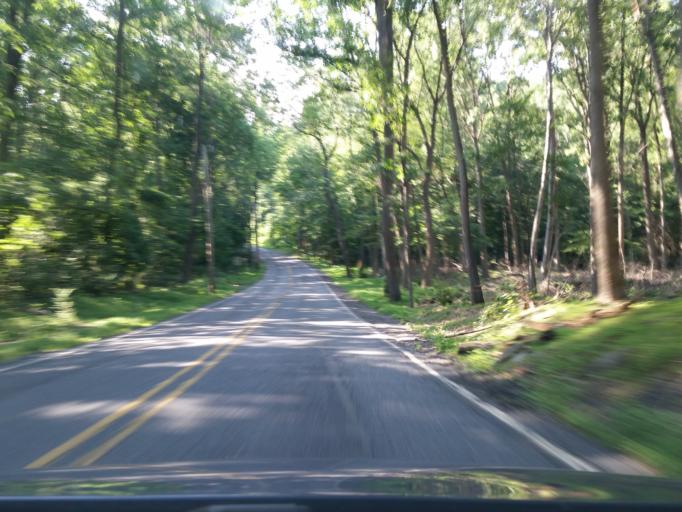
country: US
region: Pennsylvania
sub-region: Lebanon County
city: Campbelltown
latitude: 40.2324
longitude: -76.5059
